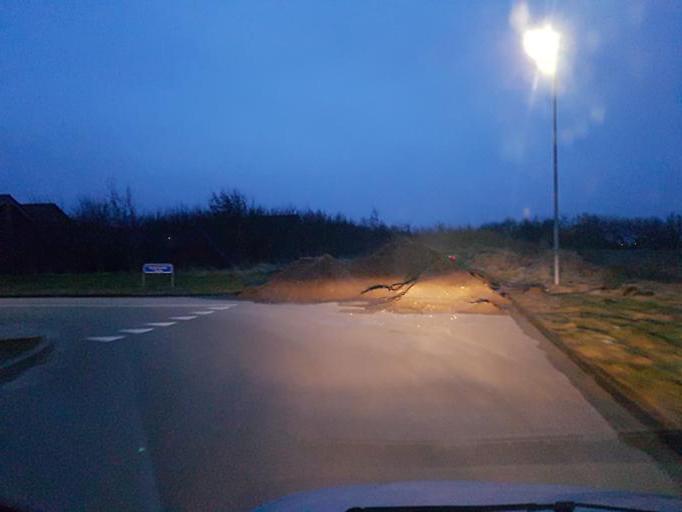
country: DK
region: South Denmark
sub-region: Esbjerg Kommune
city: Bramming
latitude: 55.4760
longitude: 8.6816
